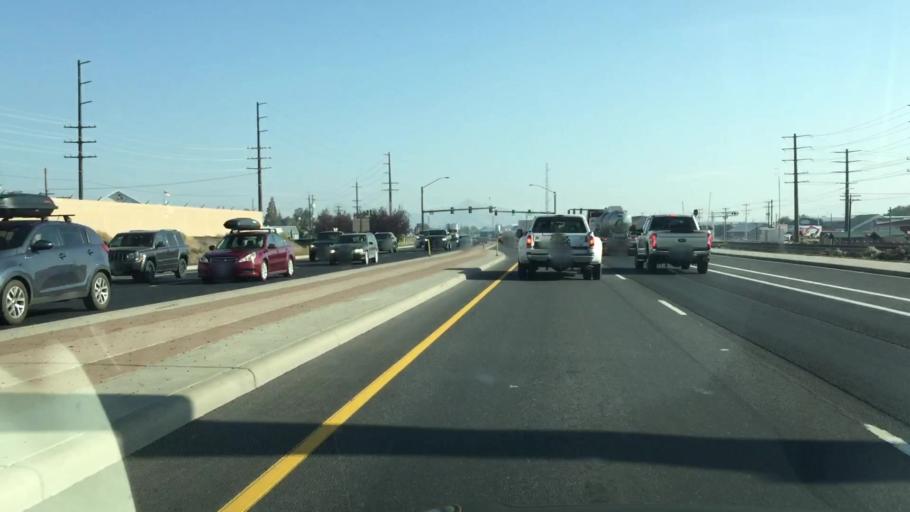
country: US
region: Oregon
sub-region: Deschutes County
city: Redmond
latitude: 44.2710
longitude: -121.1707
